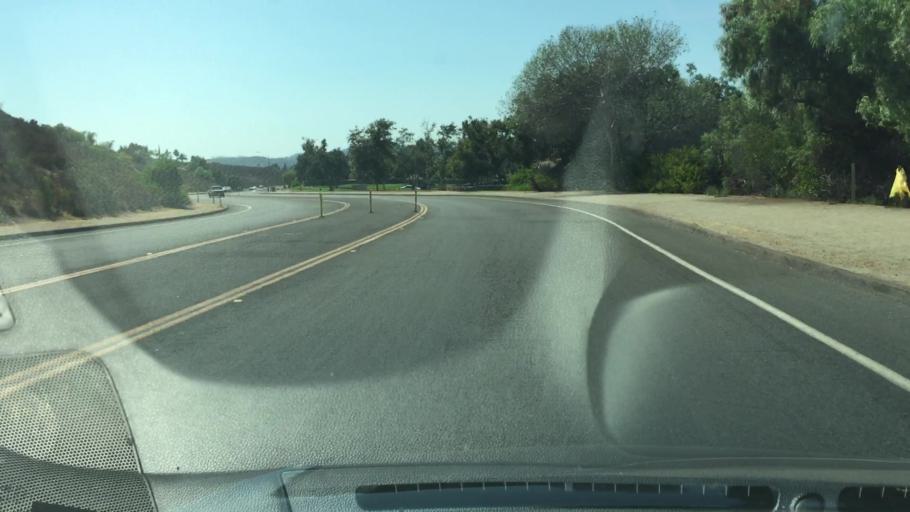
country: US
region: California
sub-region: San Diego County
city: Jamul
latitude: 32.7389
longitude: -116.8955
